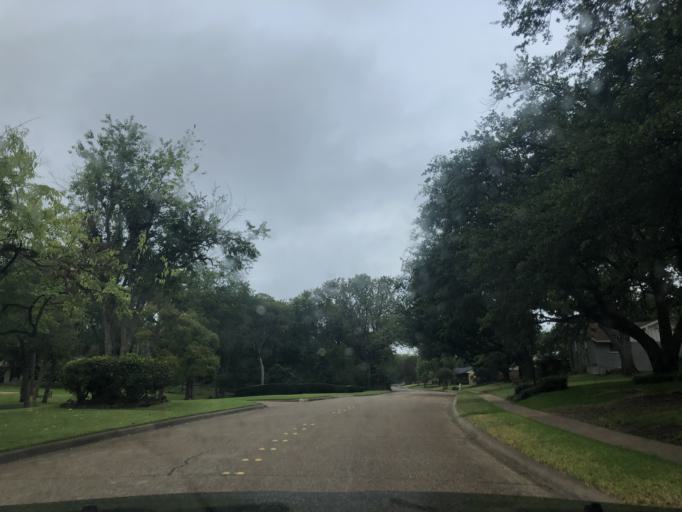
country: US
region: Texas
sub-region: Dallas County
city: Garland
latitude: 32.8726
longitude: -96.6375
